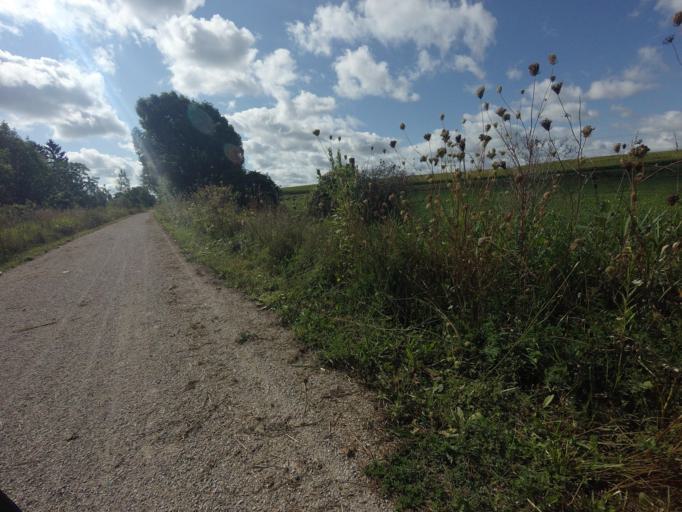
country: CA
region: Ontario
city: Huron East
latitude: 43.7316
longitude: -81.4153
